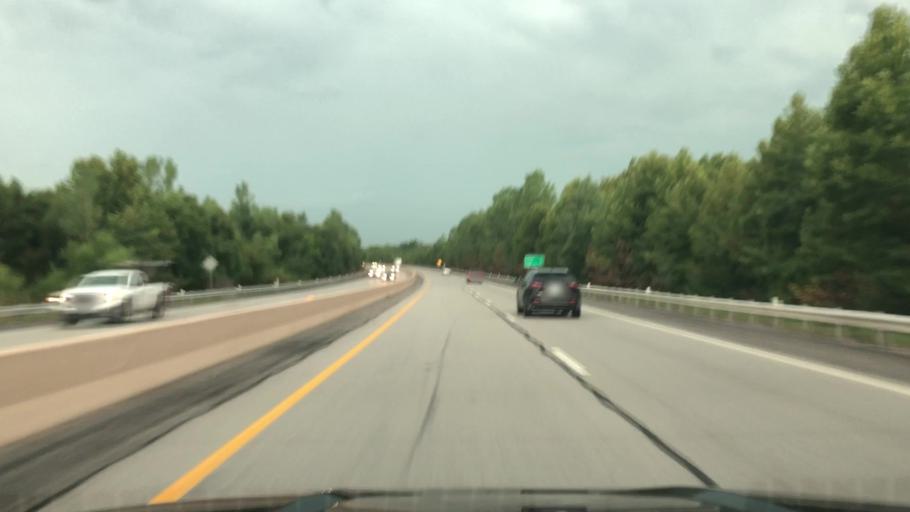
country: US
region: Oklahoma
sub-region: Rogers County
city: Claremore
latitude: 36.2946
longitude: -95.6058
